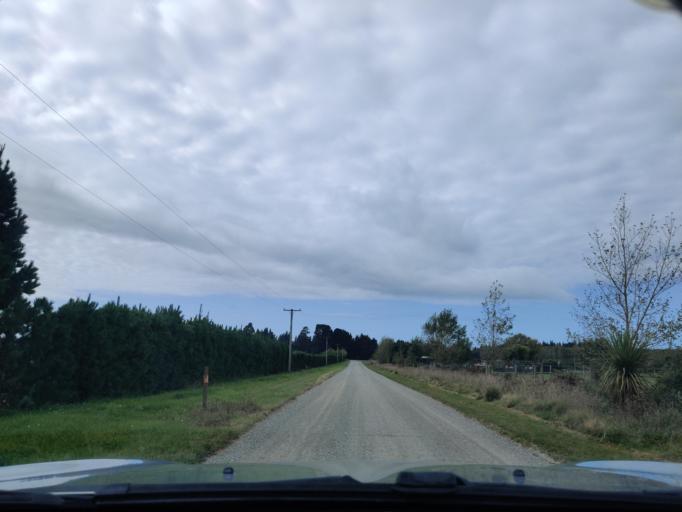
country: NZ
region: Canterbury
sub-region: Hurunui District
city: Amberley
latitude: -43.2287
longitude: 172.7140
